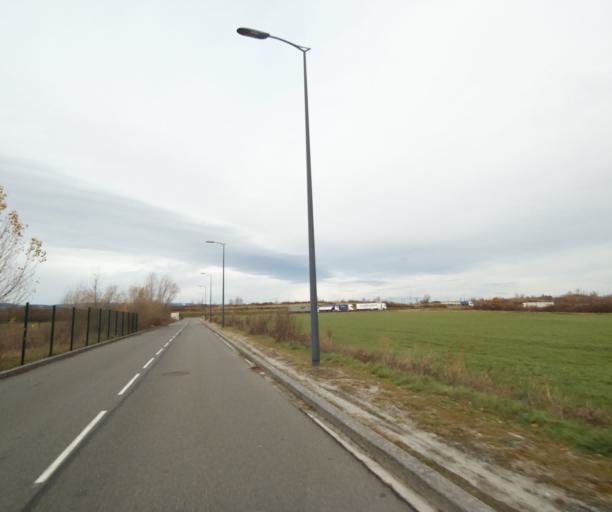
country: FR
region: Rhone-Alpes
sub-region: Departement de la Loire
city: Sury-le-Comtal
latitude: 45.5182
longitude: 4.1939
